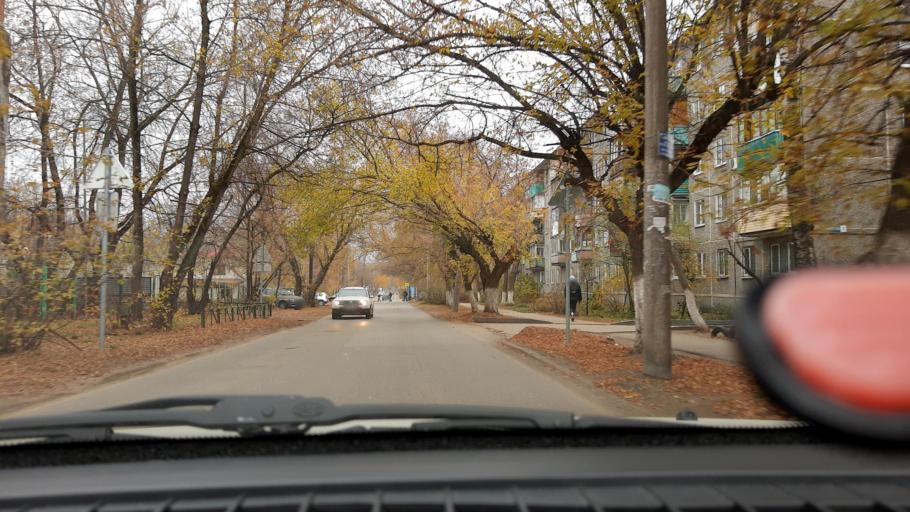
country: RU
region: Nizjnij Novgorod
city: Gorbatovka
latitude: 56.3520
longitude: 43.8385
